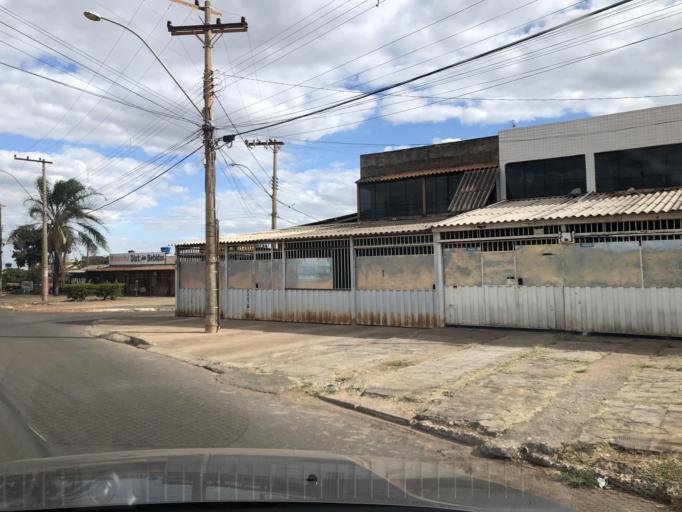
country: BR
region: Federal District
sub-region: Brasilia
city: Brasilia
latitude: -15.8869
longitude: -48.1028
